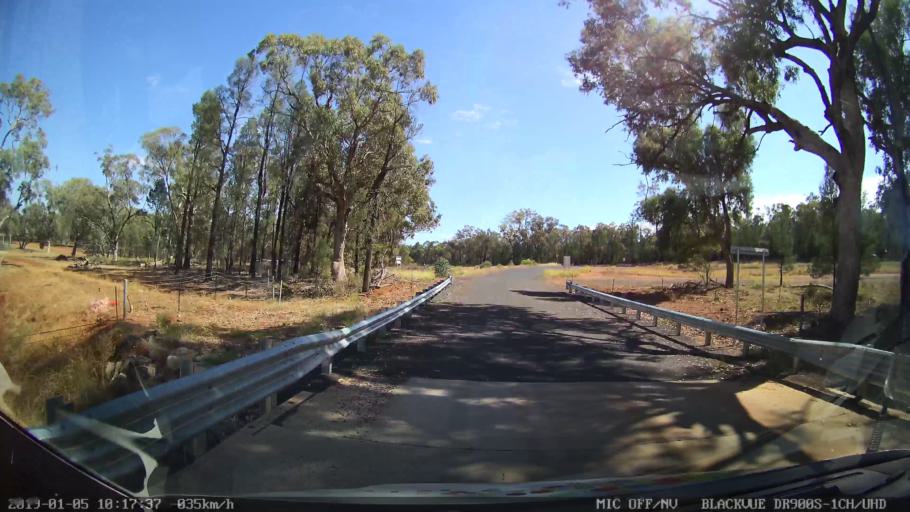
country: AU
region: New South Wales
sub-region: Gilgandra
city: Gilgandra
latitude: -31.5658
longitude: 148.9610
